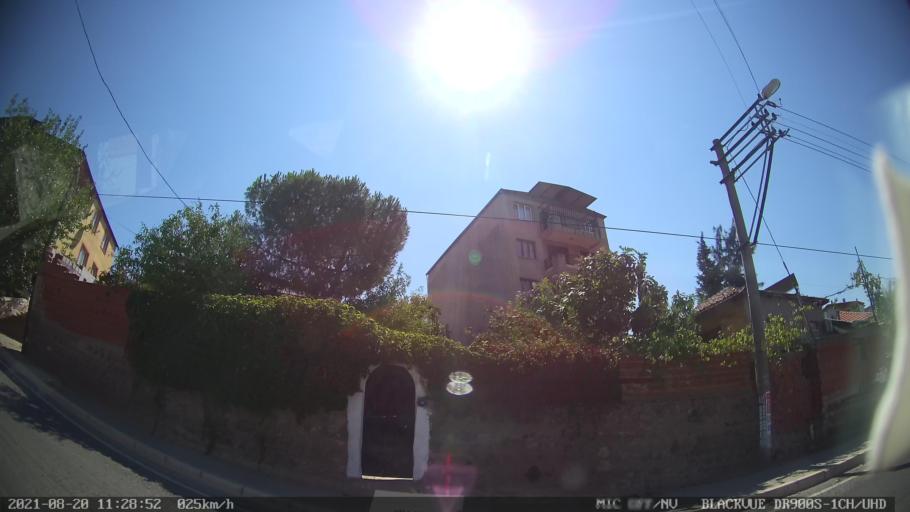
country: TR
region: Izmir
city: Karsiyaka
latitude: 38.4994
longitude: 27.0696
